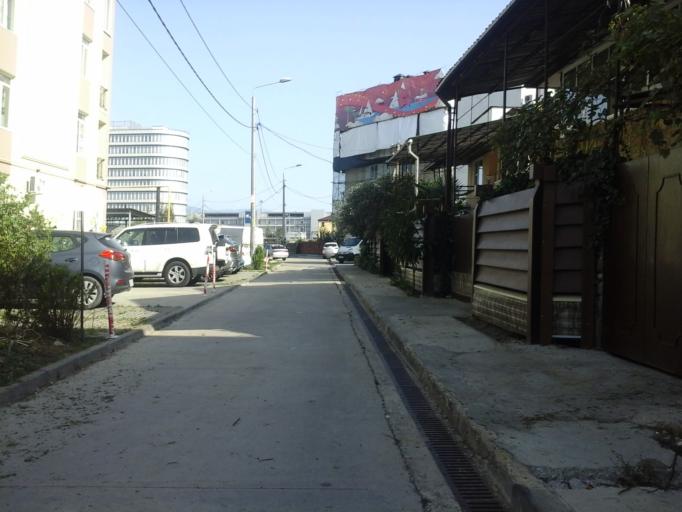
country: RU
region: Krasnodarskiy
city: Adler
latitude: 43.4125
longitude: 39.9625
